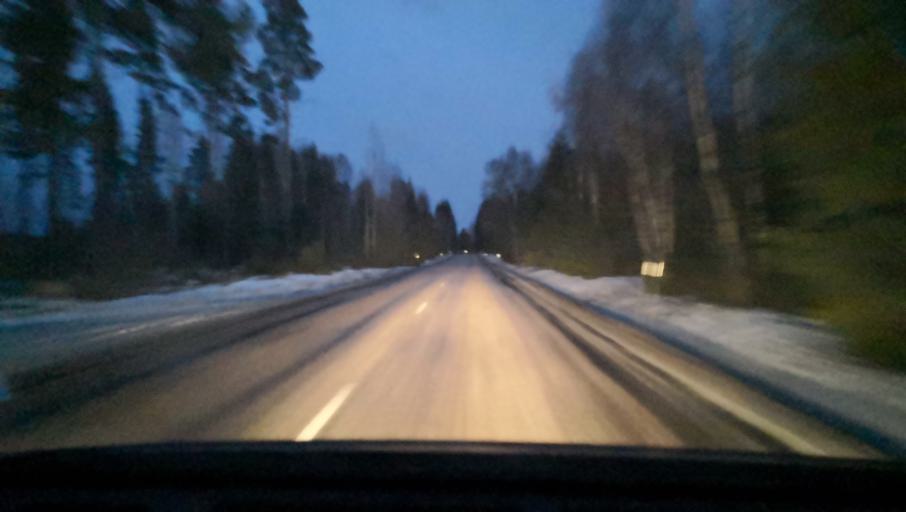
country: SE
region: Vaestmanland
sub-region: Sala Kommun
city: Sala
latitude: 59.8365
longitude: 16.5019
